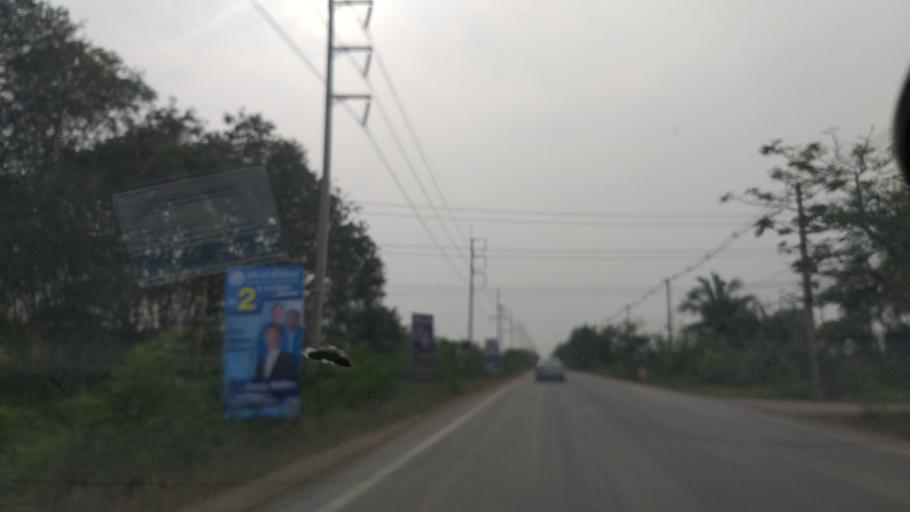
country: TH
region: Chachoengsao
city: Ban Pho
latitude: 13.6006
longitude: 101.1628
